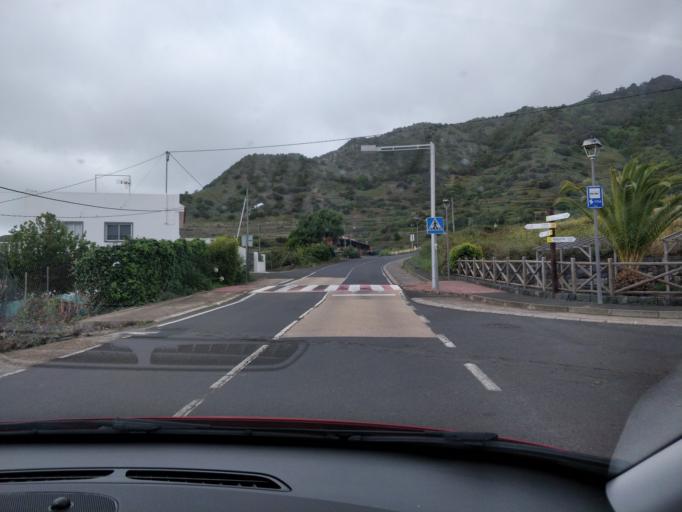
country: ES
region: Canary Islands
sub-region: Provincia de Santa Cruz de Tenerife
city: Tanque
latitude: 28.3290
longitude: -16.8458
